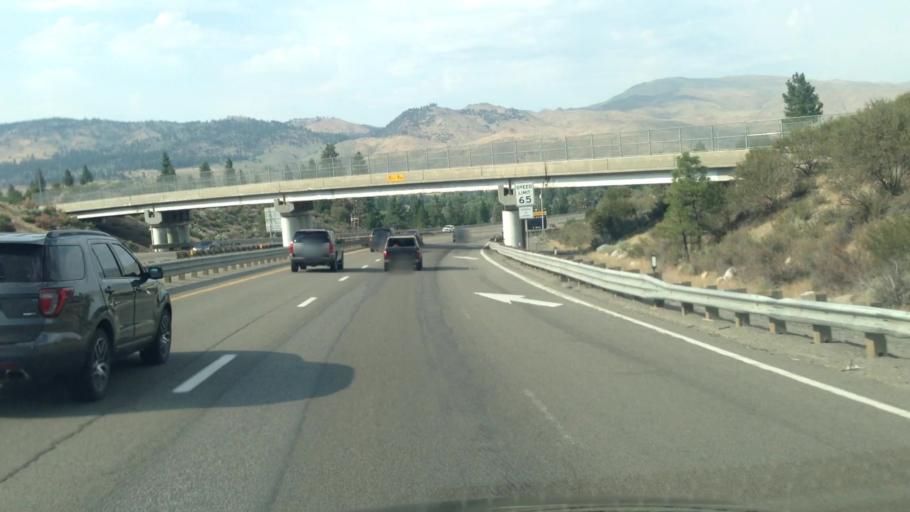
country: US
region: Nevada
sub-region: Washoe County
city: Verdi
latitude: 39.5061
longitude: -119.9990
